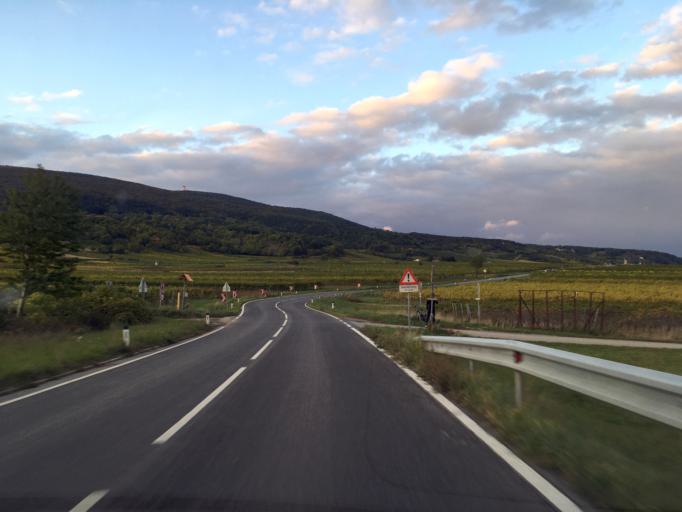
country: AT
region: Lower Austria
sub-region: Politischer Bezirk Baden
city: Pfaffstatten
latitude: 48.0293
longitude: 16.2626
